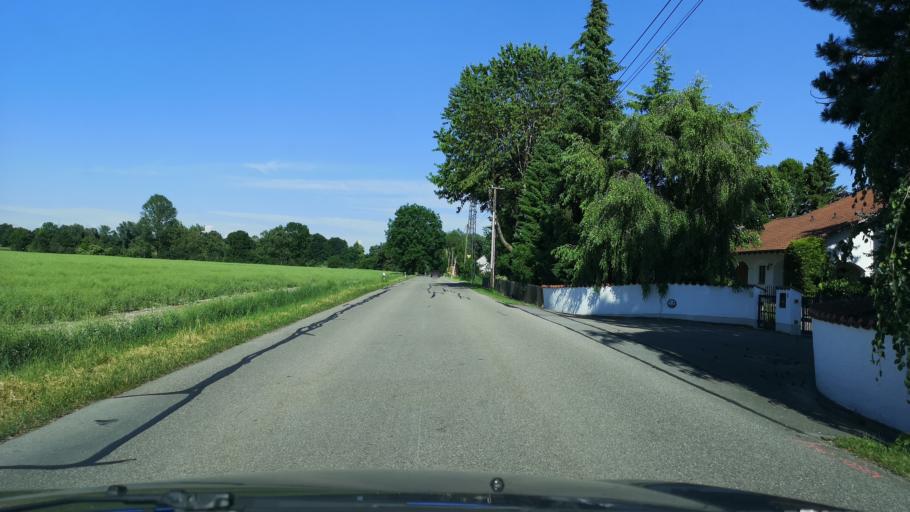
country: DE
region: Bavaria
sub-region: Upper Bavaria
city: Eichenried
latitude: 48.2648
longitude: 11.7504
